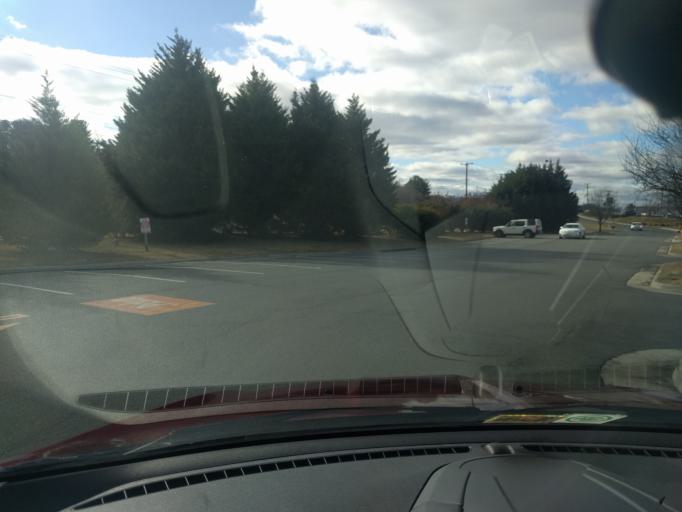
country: US
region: Virginia
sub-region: City of Bedford
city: Bedford
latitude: 37.3245
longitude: -79.4980
